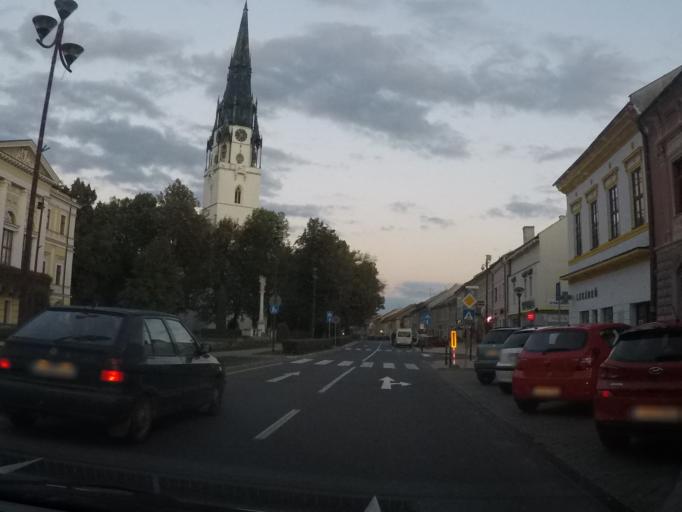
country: SK
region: Kosicky
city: Spisska Nova Ves
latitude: 48.9440
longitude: 20.5664
